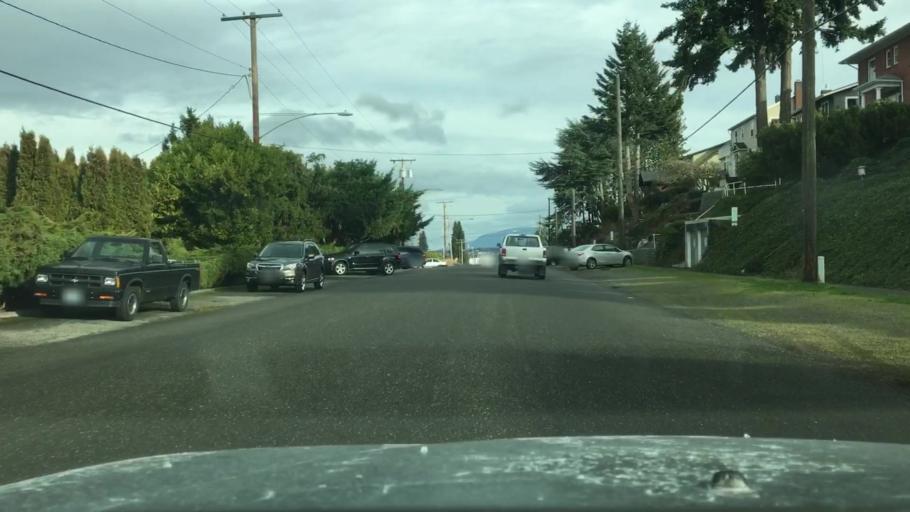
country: US
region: Washington
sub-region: Whatcom County
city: Bellingham
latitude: 48.7393
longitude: -122.4905
